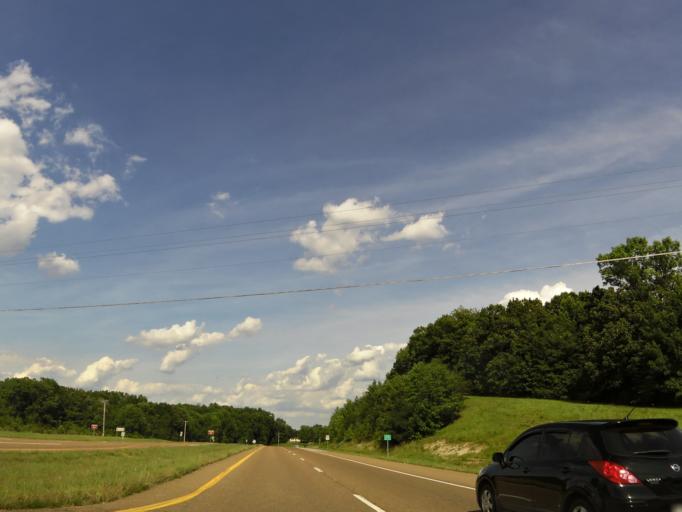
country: US
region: Tennessee
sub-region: Carroll County
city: Huntingdon
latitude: 36.0252
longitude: -88.4075
